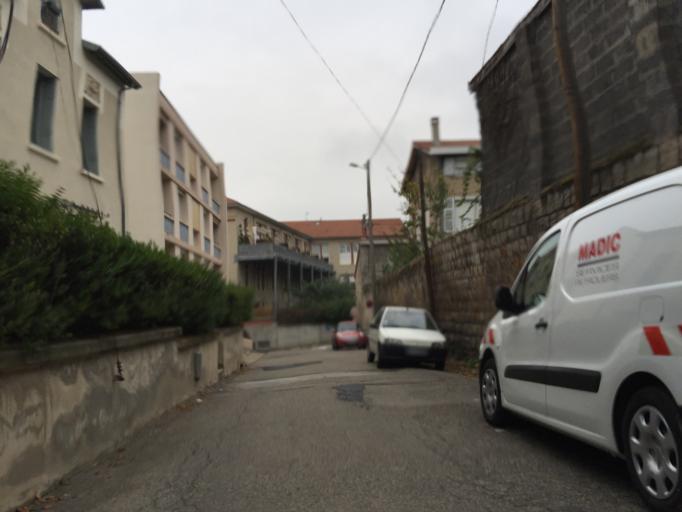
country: FR
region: Rhone-Alpes
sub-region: Departement de la Loire
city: Saint-Chamond
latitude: 45.4726
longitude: 4.5135
